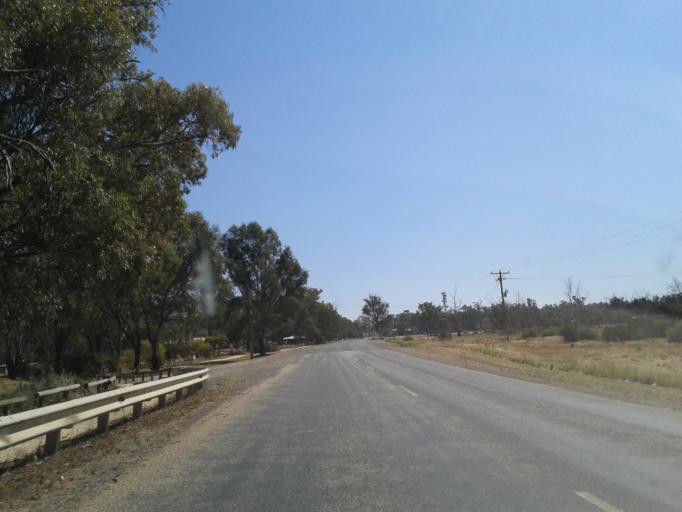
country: AU
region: Victoria
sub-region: Swan Hill
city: Swan Hill
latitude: -35.3367
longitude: 143.5720
